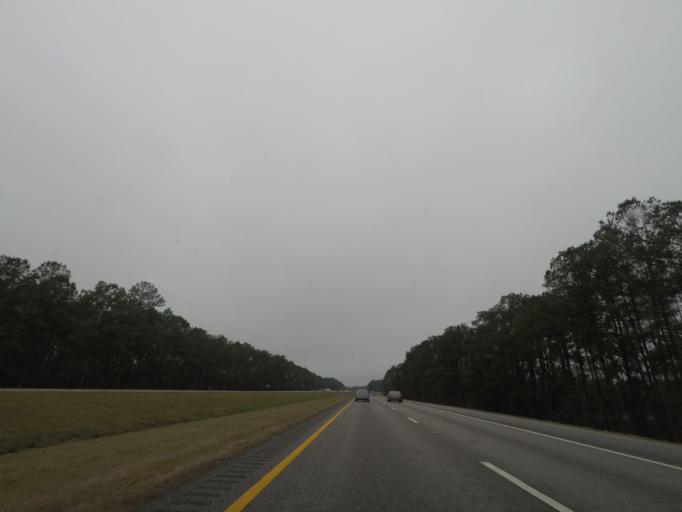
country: US
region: South Carolina
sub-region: Sumter County
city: East Sumter
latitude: 33.9079
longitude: -80.0894
